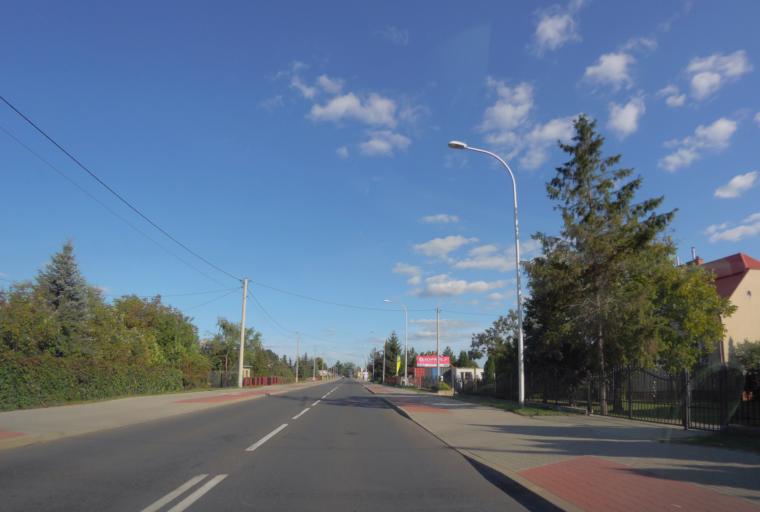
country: PL
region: Subcarpathian Voivodeship
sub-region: Tarnobrzeg
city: Tarnobrzeg
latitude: 50.5692
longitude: 21.7083
